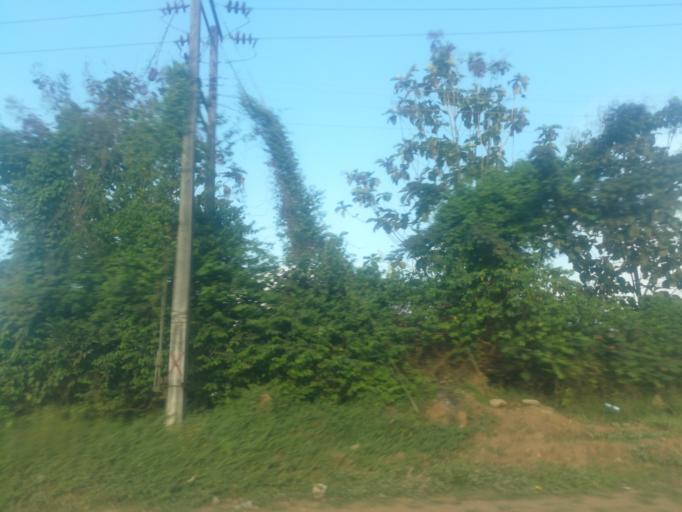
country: NG
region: Oyo
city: Moniya
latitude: 7.5402
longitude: 3.8996
